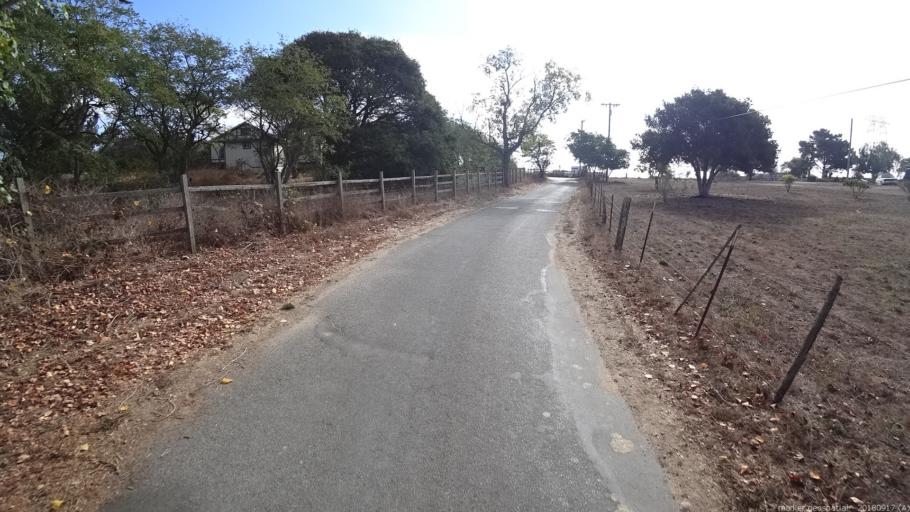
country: US
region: California
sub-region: Monterey County
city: Castroville
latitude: 36.7866
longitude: -121.7210
